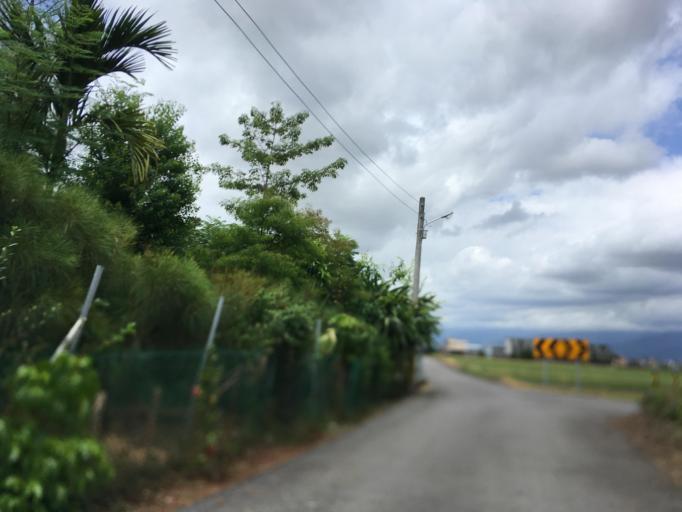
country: TW
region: Taiwan
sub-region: Yilan
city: Yilan
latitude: 24.6920
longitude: 121.7270
